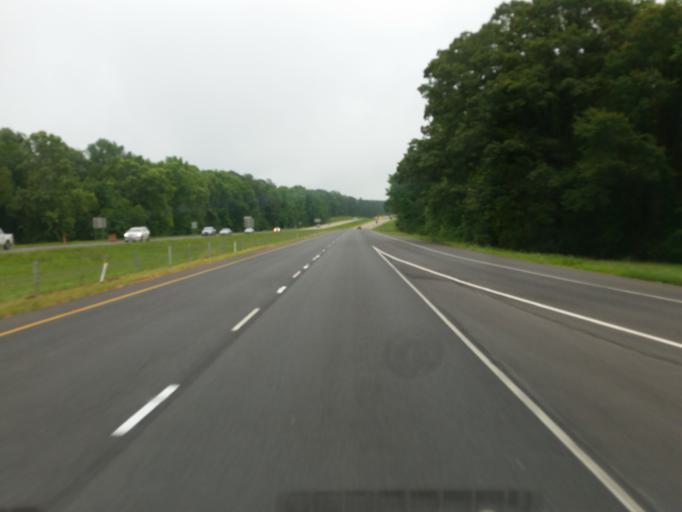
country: US
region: Louisiana
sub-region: Bienville Parish
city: Arcadia
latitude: 32.5632
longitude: -93.0523
